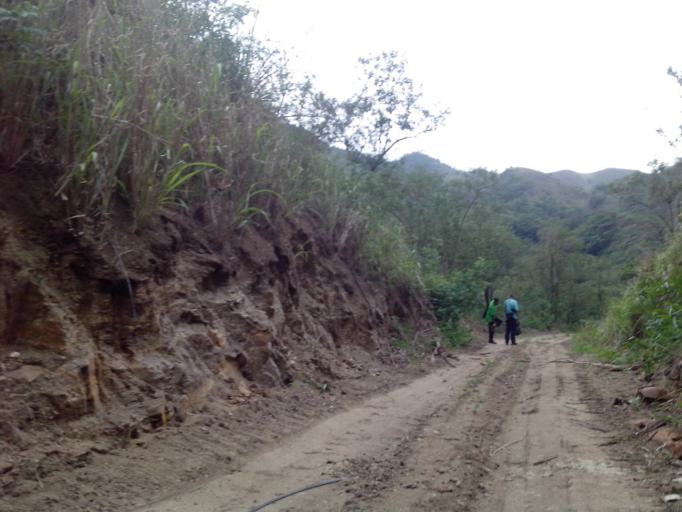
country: BR
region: Rio de Janeiro
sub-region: Miguel Pereira
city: Miguel Pereira
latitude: -22.5079
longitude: -43.5129
